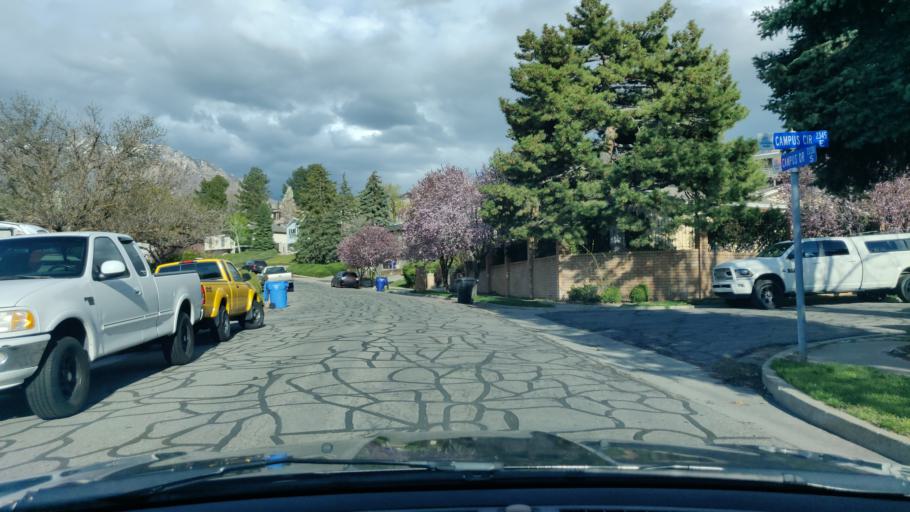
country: US
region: Utah
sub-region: Salt Lake County
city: Cottonwood Heights
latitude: 40.6198
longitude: -111.8239
